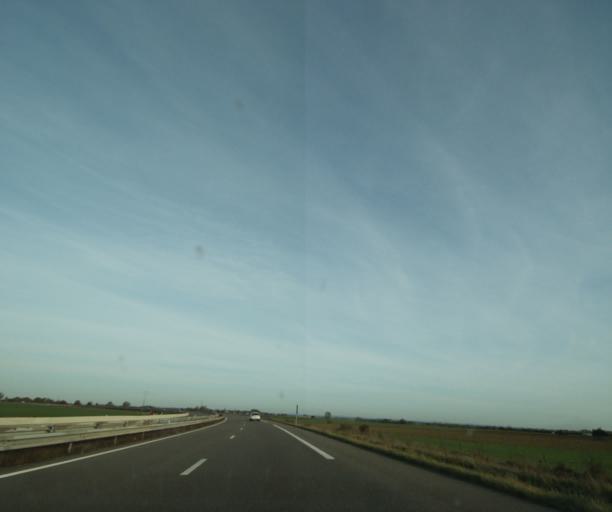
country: FR
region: Lorraine
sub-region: Departement de la Meuse
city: Etain
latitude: 49.1103
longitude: 5.5658
